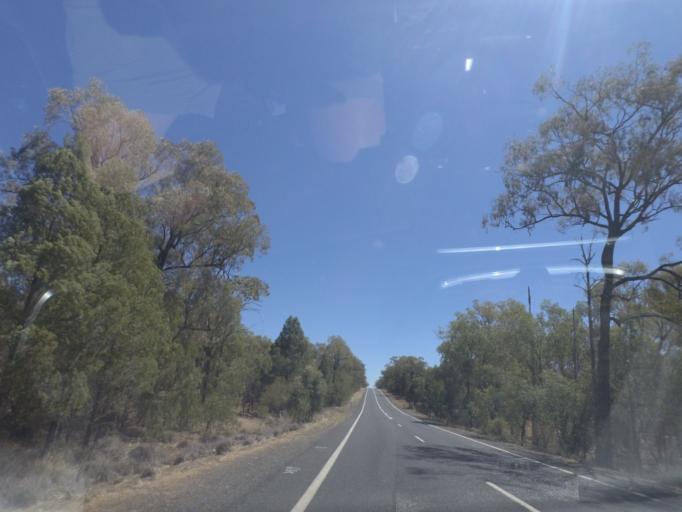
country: AU
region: New South Wales
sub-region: Gilgandra
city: Gilgandra
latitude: -31.4839
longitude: 148.8829
